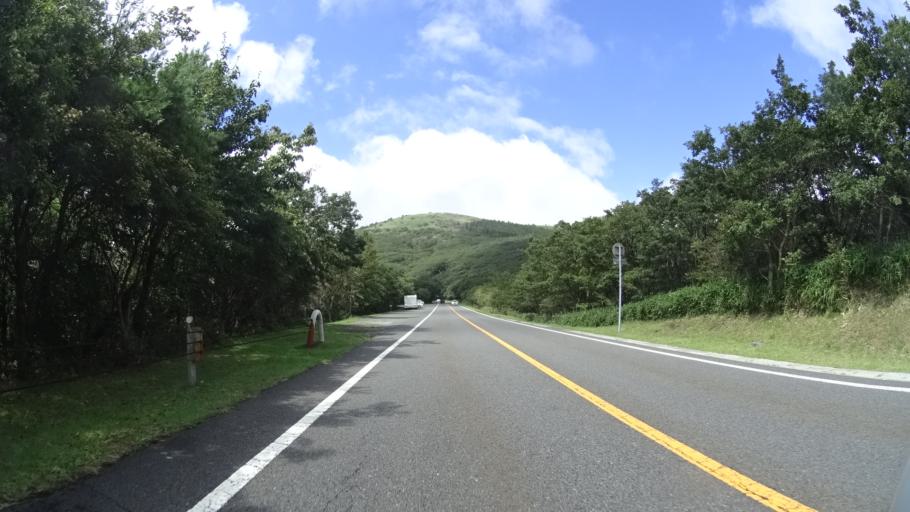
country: JP
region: Oita
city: Tsukawaki
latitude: 33.0950
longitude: 131.2021
